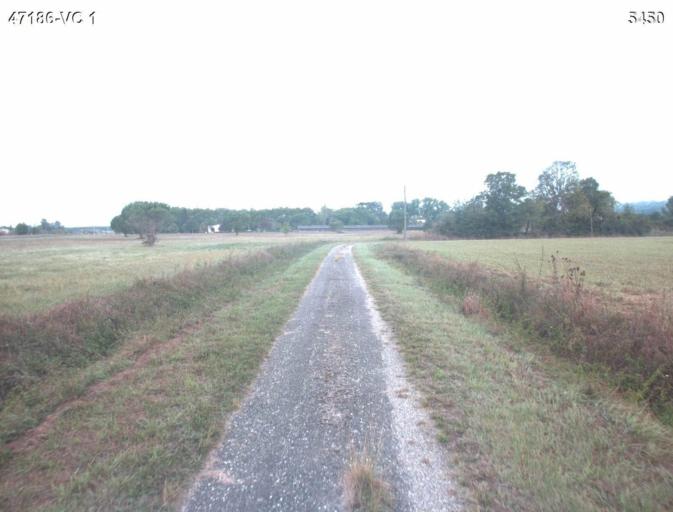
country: FR
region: Aquitaine
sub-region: Departement du Lot-et-Garonne
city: Port-Sainte-Marie
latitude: 44.2309
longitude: 0.4319
